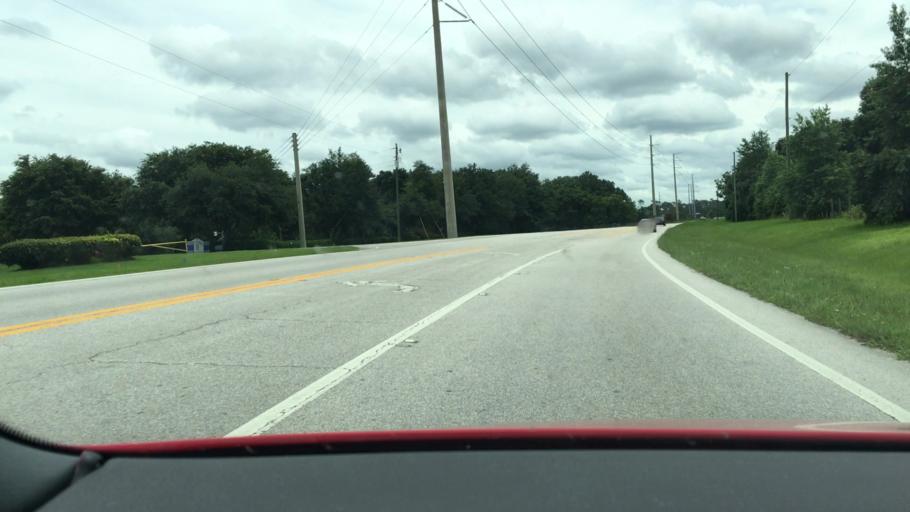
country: US
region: Florida
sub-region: Lake County
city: Eustis
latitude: 28.8747
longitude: -81.6688
